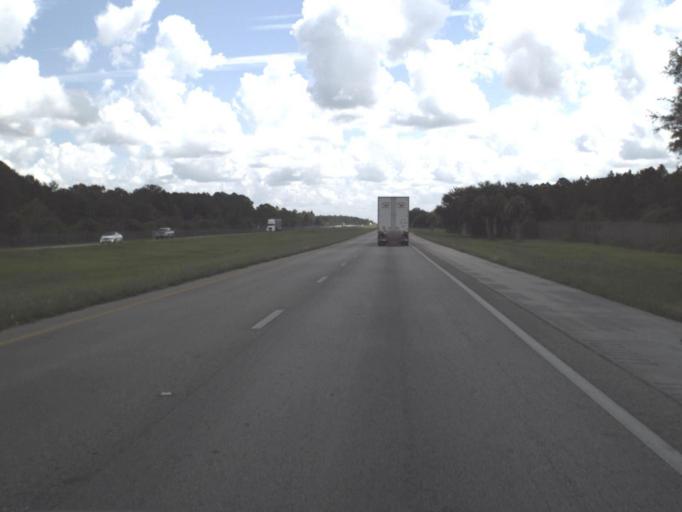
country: US
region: Florida
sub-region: Collier County
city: Orangetree
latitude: 26.1530
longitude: -81.4901
